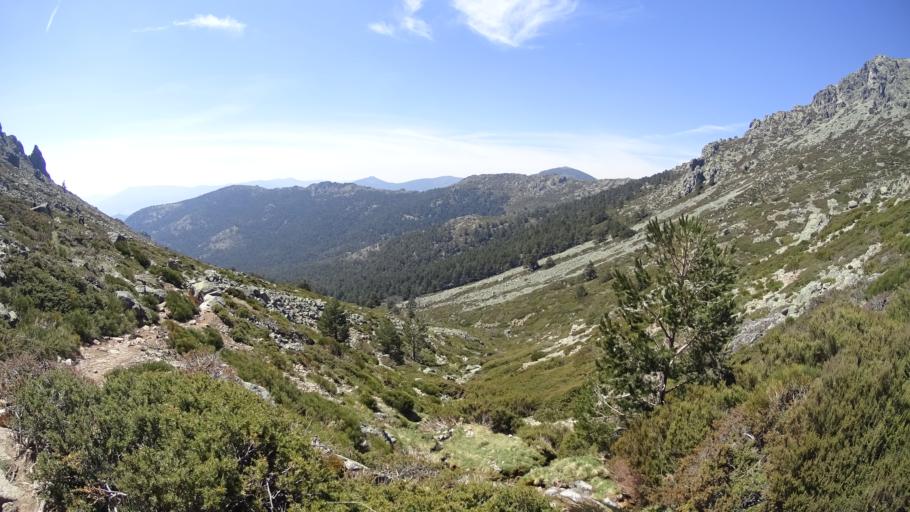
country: ES
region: Madrid
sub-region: Provincia de Madrid
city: Becerril de la Sierra
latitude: 40.7743
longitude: -3.9794
